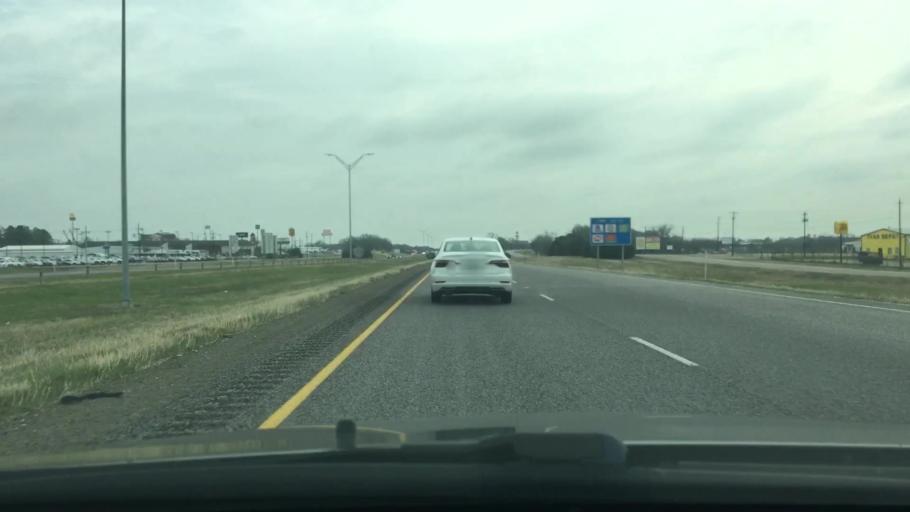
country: US
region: Texas
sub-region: Freestone County
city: Fairfield
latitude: 31.7237
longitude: -96.1795
